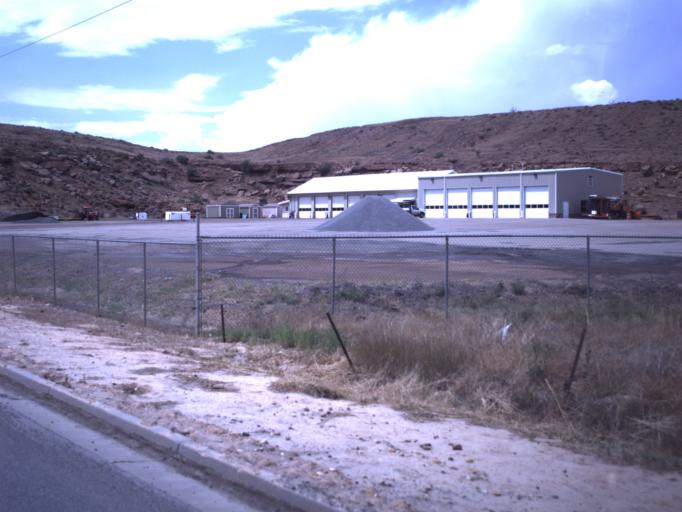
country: US
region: Utah
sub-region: Duchesne County
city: Roosevelt
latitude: 40.2905
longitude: -109.9969
